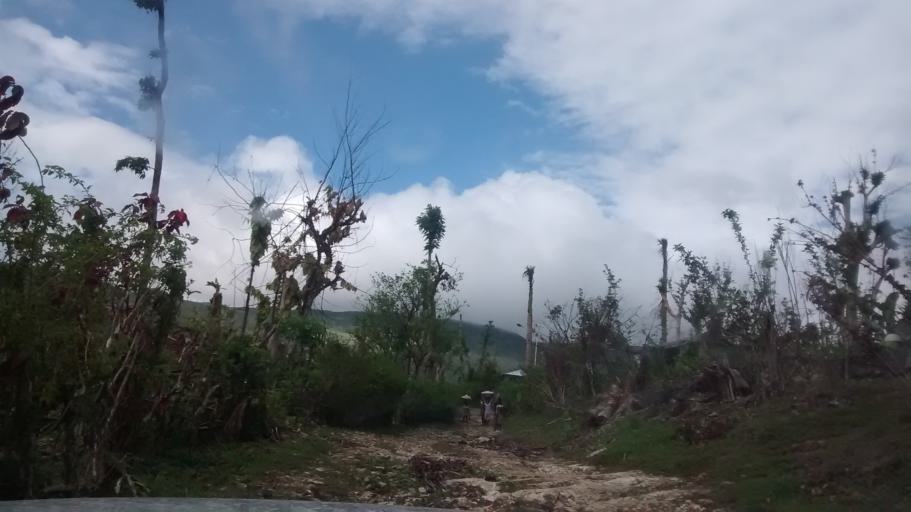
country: HT
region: Grandans
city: Moron
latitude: 18.5600
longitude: -74.2708
